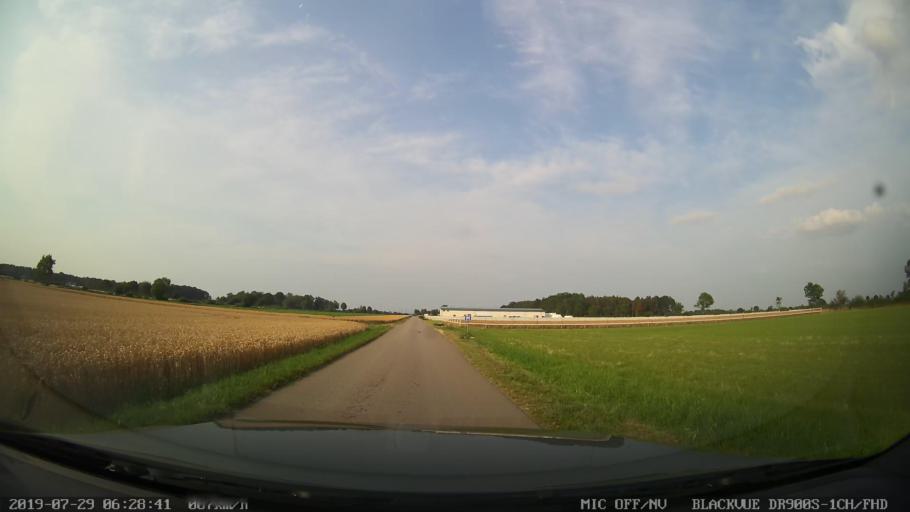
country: SE
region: Skane
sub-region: Helsingborg
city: Odakra
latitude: 56.1149
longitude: 12.7206
